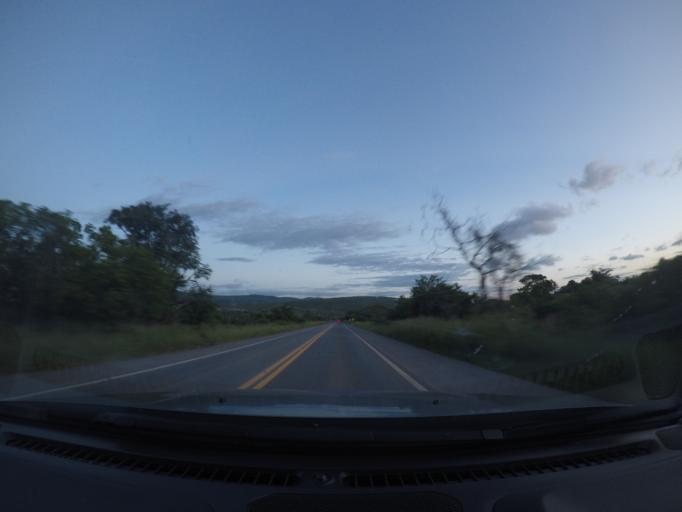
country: BR
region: Bahia
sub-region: Seabra
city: Seabra
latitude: -12.4862
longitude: -41.7349
